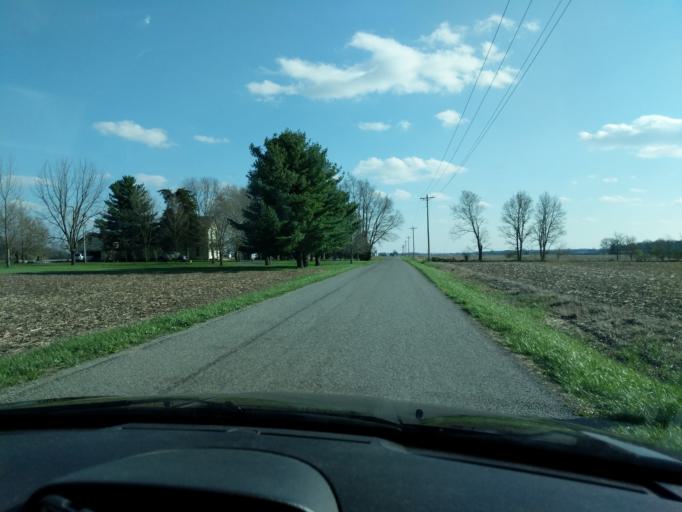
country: US
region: Ohio
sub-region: Champaign County
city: Urbana
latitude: 40.1276
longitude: -83.8111
